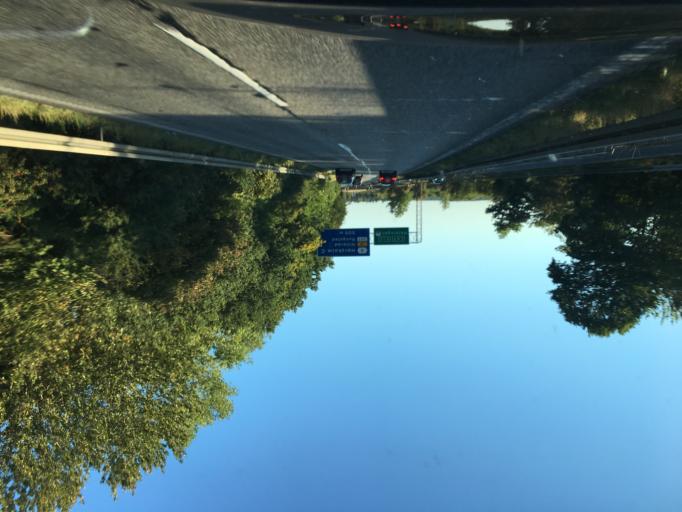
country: DK
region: Capital Region
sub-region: Horsholm Kommune
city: Horsholm
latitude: 55.8676
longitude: 12.4837
